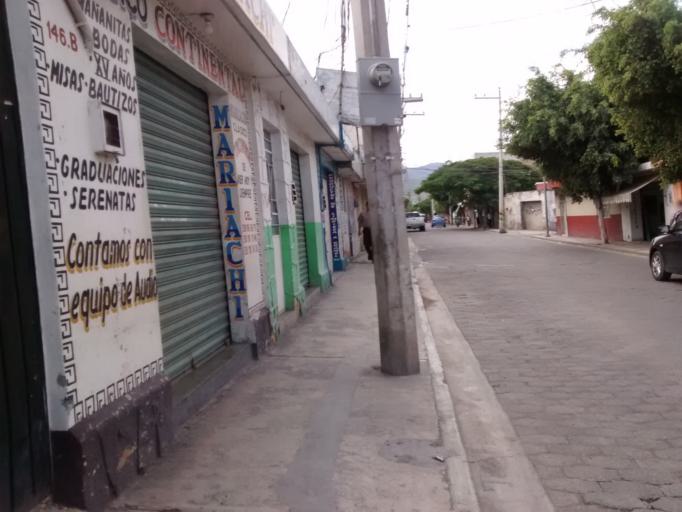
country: MX
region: Puebla
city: Tehuacan
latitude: 18.4610
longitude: -97.3871
